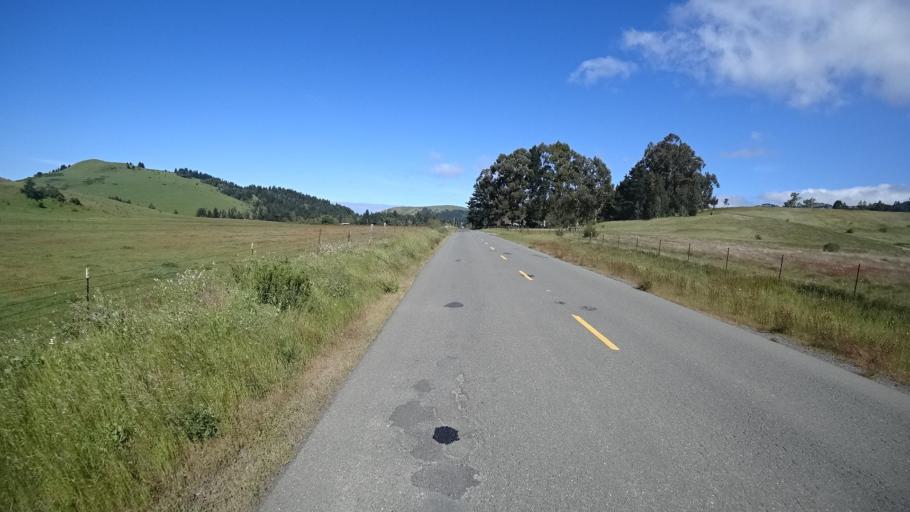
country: US
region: California
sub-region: Humboldt County
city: Ferndale
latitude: 40.3379
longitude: -124.3114
